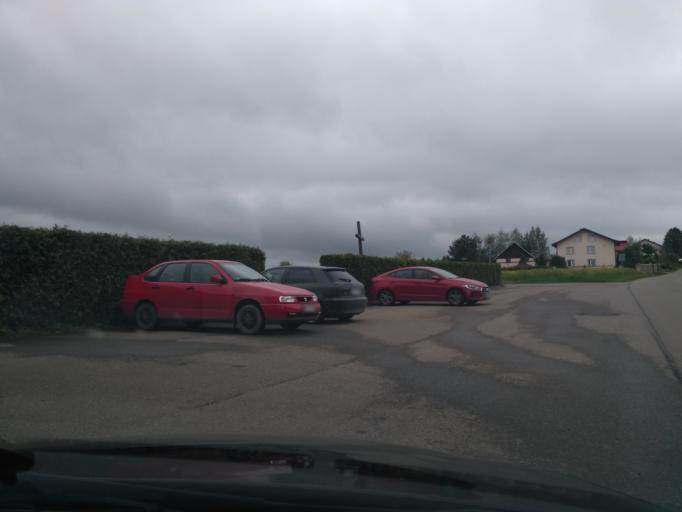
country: PL
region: Subcarpathian Voivodeship
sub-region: Powiat strzyzowski
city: Frysztak
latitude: 49.8025
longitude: 21.5406
